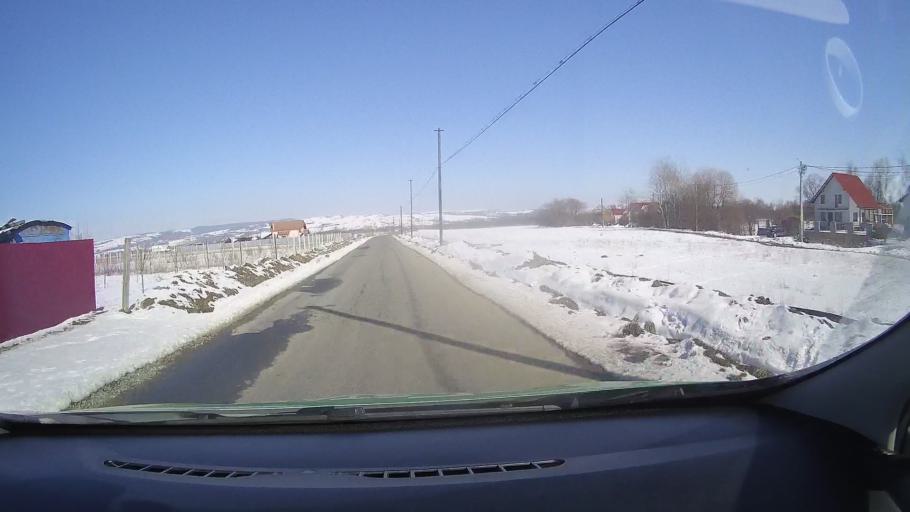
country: RO
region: Brasov
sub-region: Comuna Mandra
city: Mandra
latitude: 45.8262
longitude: 25.0100
